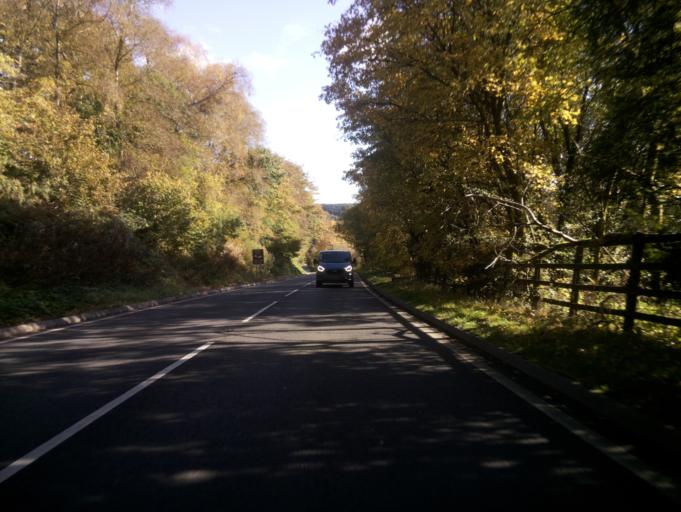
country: GB
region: Wales
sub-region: Rhondda Cynon Taf
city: Hirwaun
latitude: 51.8275
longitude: -3.4539
